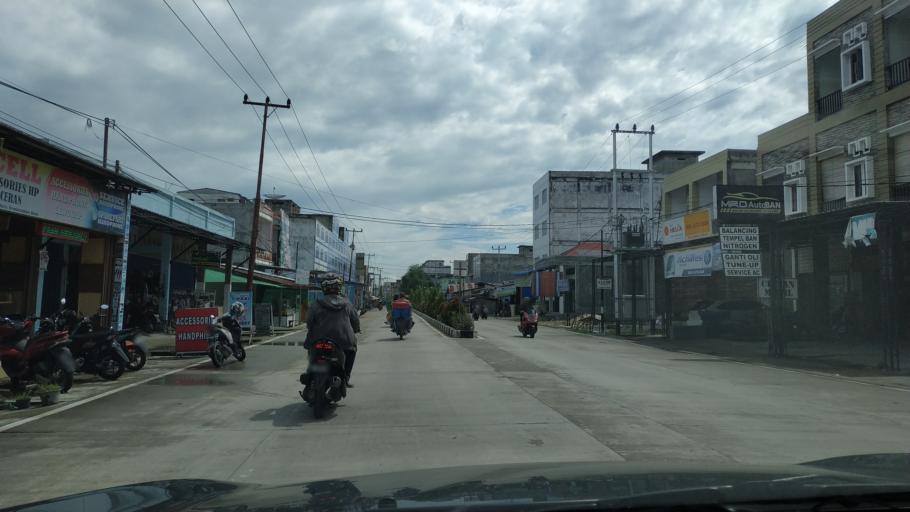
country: ID
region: Riau
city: Tembilahan
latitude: -0.3252
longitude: 103.1471
